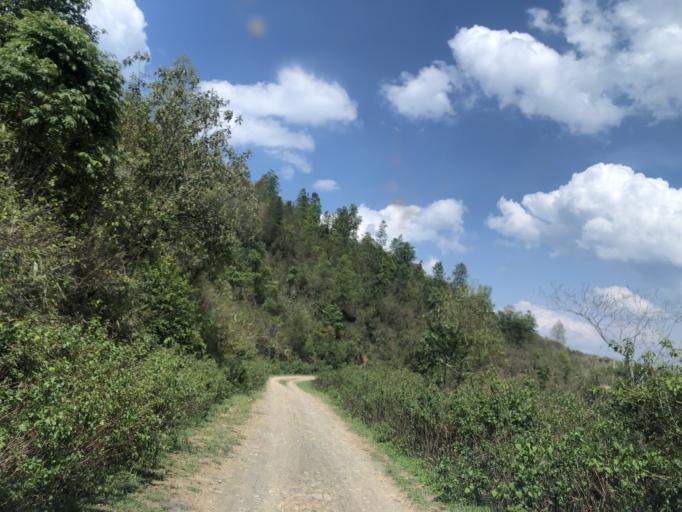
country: LA
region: Phongsali
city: Phongsali
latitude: 21.4081
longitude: 102.2349
